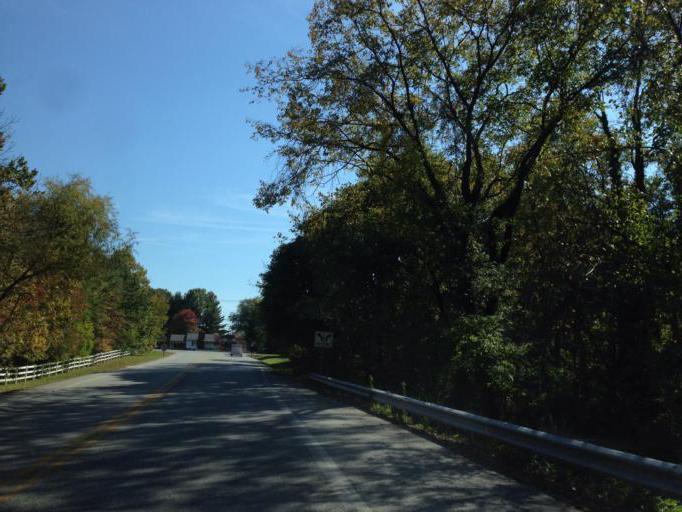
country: US
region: Maryland
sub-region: Howard County
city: Ellicott City
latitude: 39.2583
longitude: -76.8192
